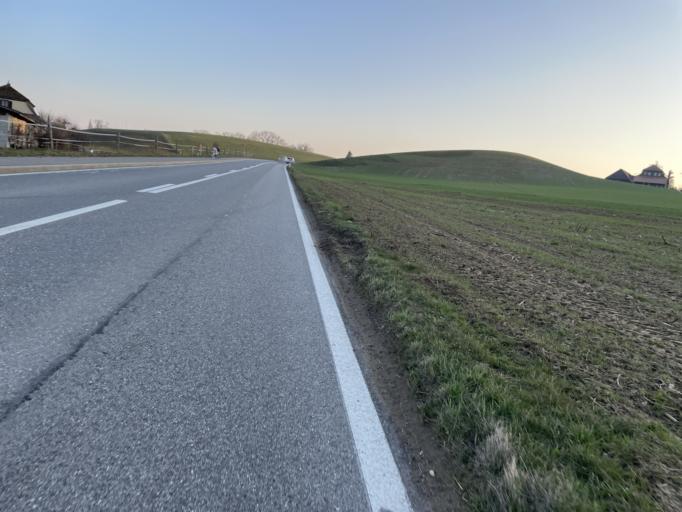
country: CH
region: Bern
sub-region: Bern-Mittelland District
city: Worb
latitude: 46.9206
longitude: 7.5668
